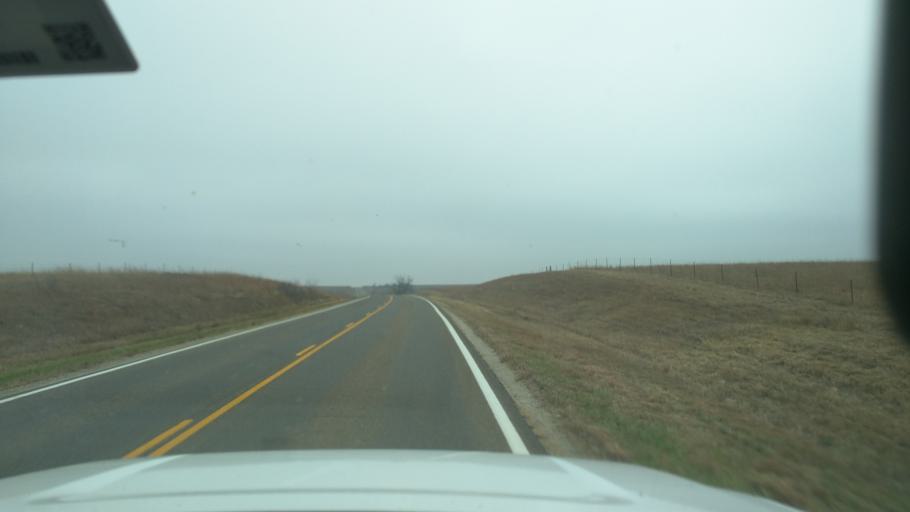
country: US
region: Kansas
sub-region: Morris County
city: Council Grove
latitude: 38.6593
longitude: -96.2681
